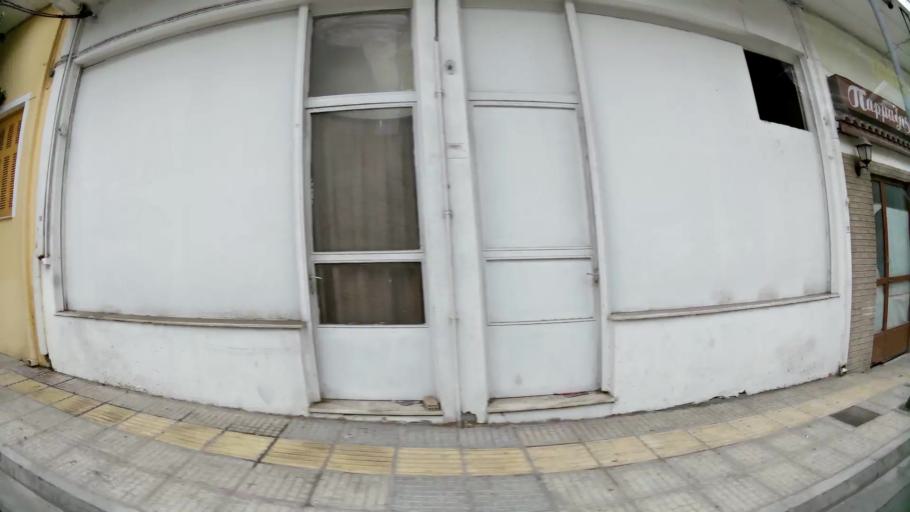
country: GR
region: Attica
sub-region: Nomarchia Athinas
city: Aigaleo
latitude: 37.9864
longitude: 23.6794
